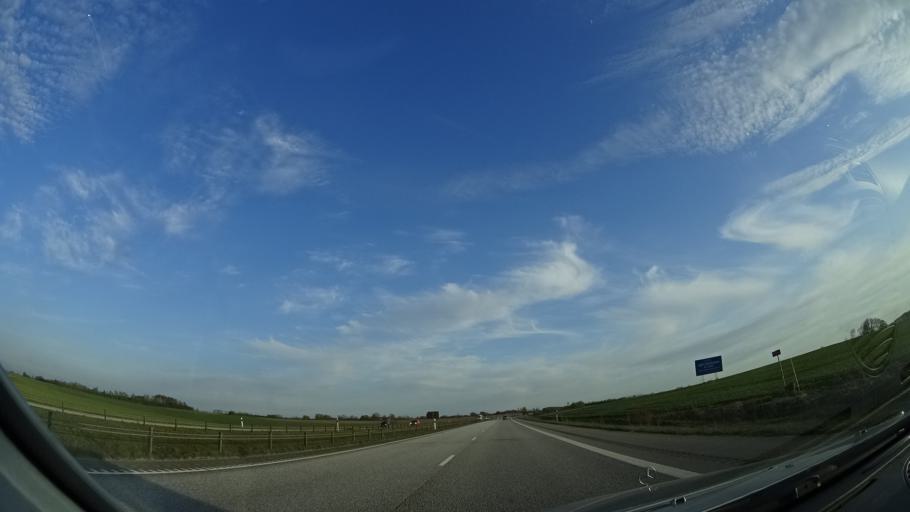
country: SE
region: Skane
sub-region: Burlovs Kommun
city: Arloev
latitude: 55.5985
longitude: 13.1170
